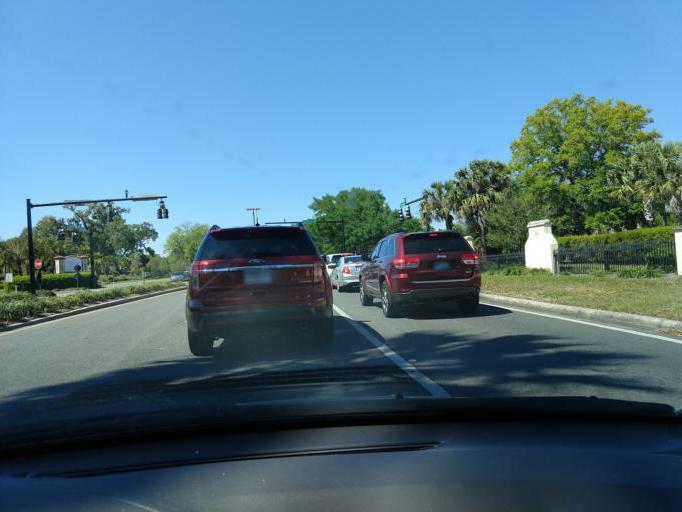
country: US
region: Florida
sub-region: Sumter County
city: The Villages
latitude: 28.9514
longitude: -81.9629
